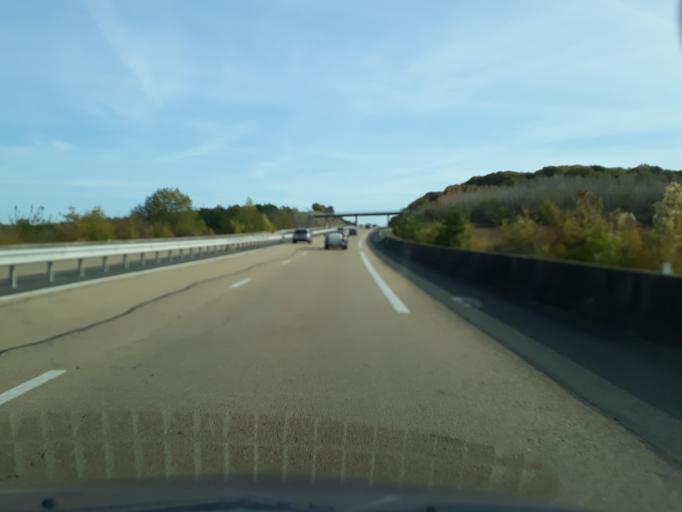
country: FR
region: Champagne-Ardenne
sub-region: Departement de l'Aube
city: Aix-en-Othe
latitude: 48.2569
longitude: 3.6399
